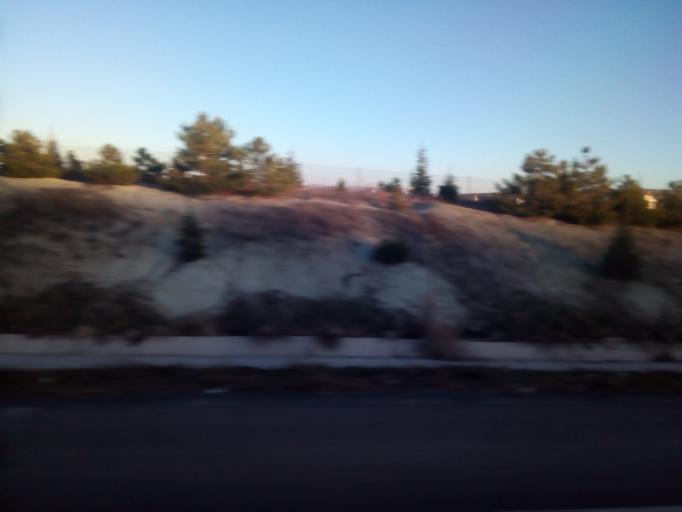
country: TR
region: Ankara
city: Etimesgut
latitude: 39.9061
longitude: 32.6267
